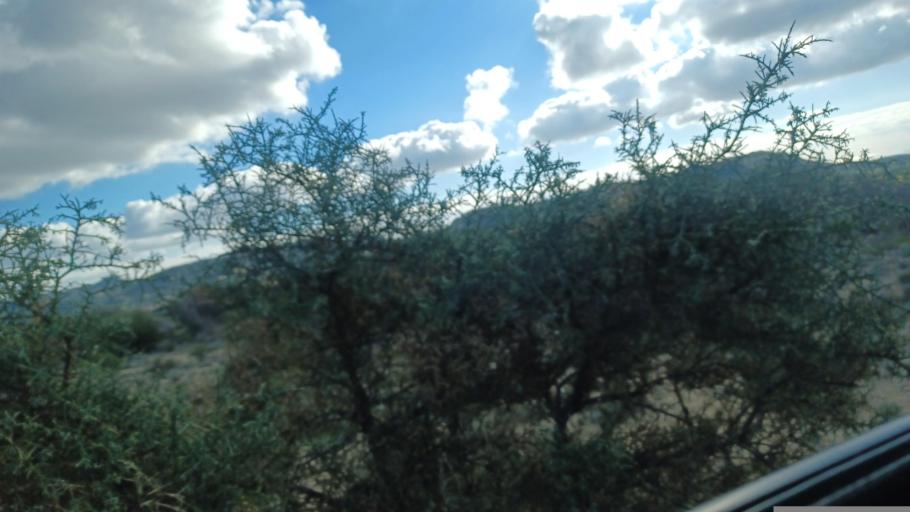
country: CY
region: Limassol
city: Pano Polemidia
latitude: 34.7655
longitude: 32.9778
